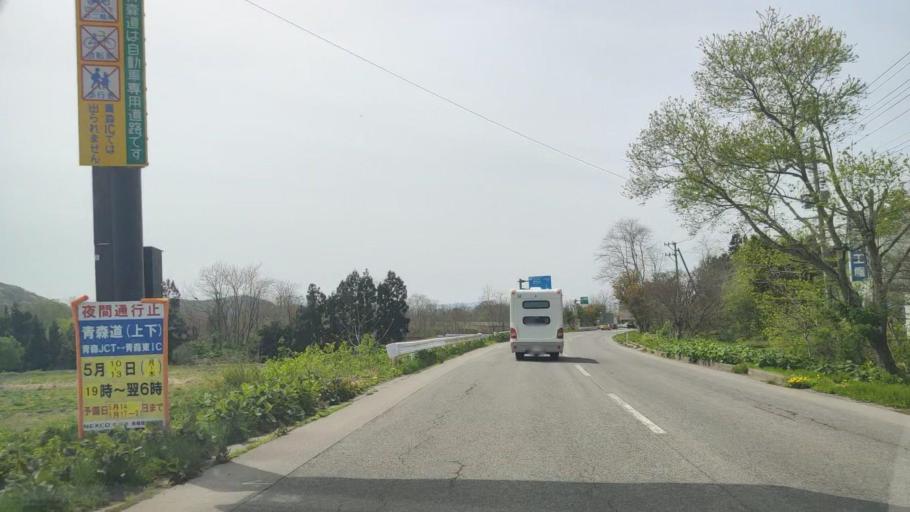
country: JP
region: Aomori
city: Aomori Shi
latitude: 40.8305
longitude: 140.8454
